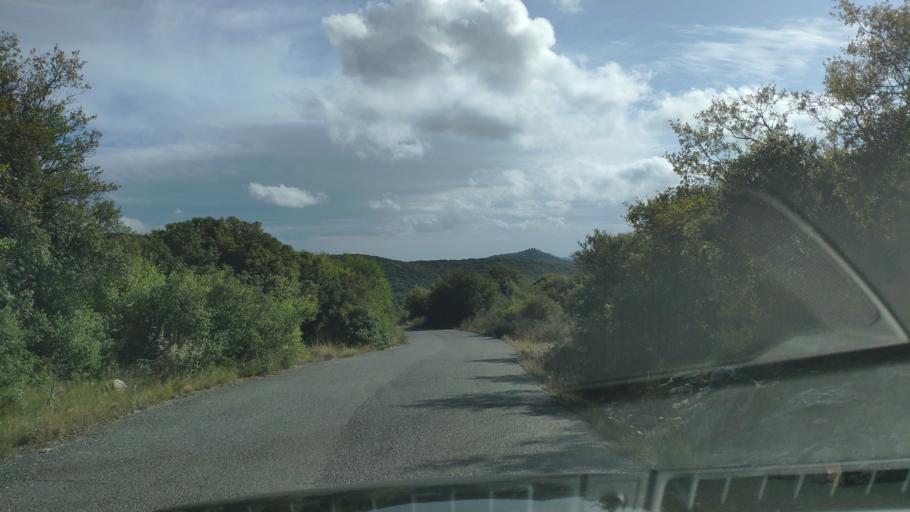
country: GR
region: Peloponnese
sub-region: Nomos Arkadias
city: Dimitsana
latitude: 37.5679
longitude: 22.0071
